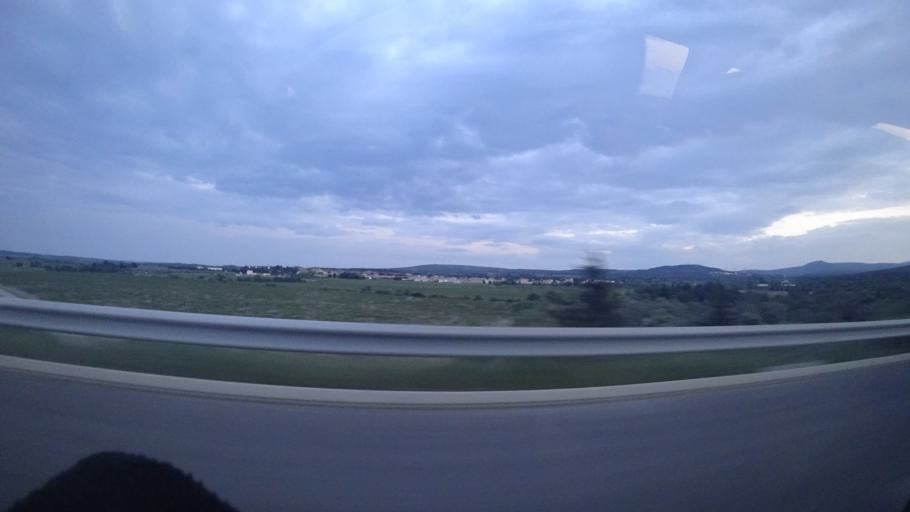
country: FR
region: Languedoc-Roussillon
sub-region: Departement de l'Aude
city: Leucate
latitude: 42.9387
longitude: 2.9763
